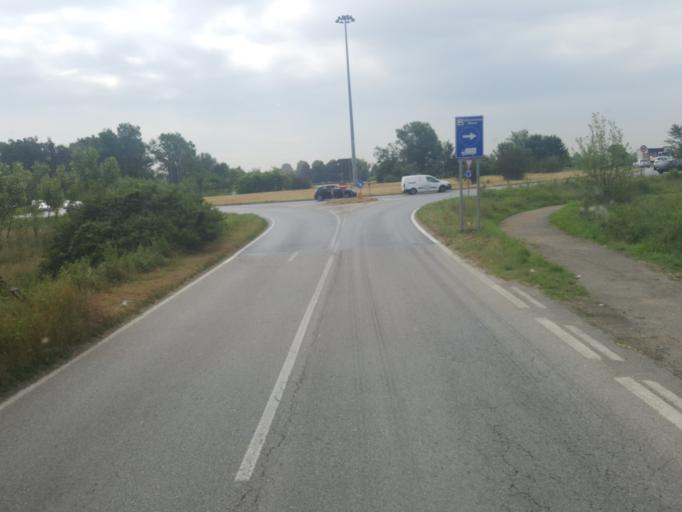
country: IT
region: Piedmont
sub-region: Provincia di Torino
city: Candiolo
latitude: 44.9630
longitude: 7.5758
